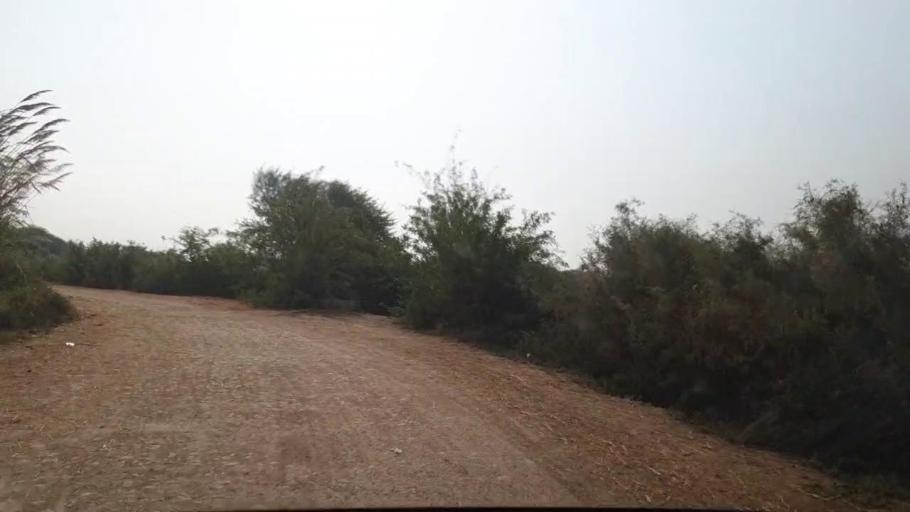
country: PK
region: Sindh
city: Chuhar Jamali
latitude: 24.3746
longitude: 67.9413
